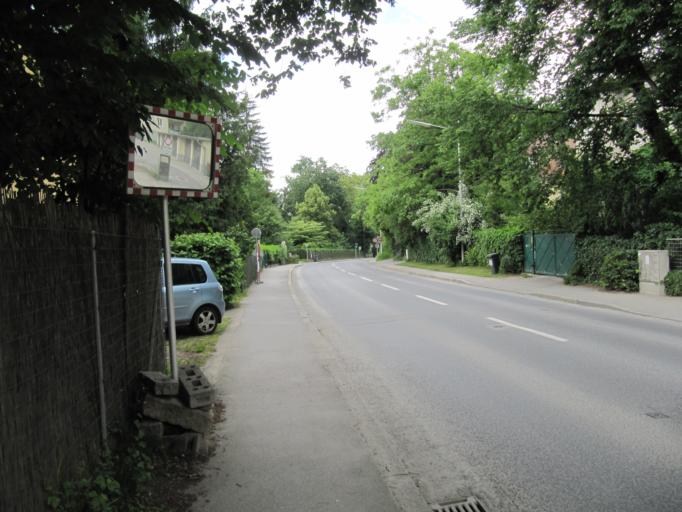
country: AT
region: Styria
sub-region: Graz Stadt
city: Graz
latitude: 47.0800
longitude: 15.4624
